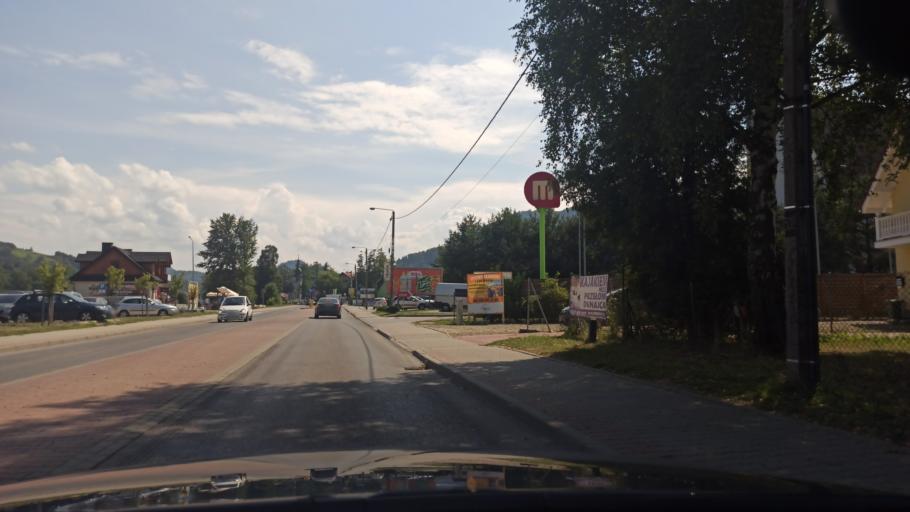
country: PL
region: Lesser Poland Voivodeship
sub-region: Powiat nowotarski
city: Kroscienko nad Dunajcem
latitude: 49.4441
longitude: 20.4258
